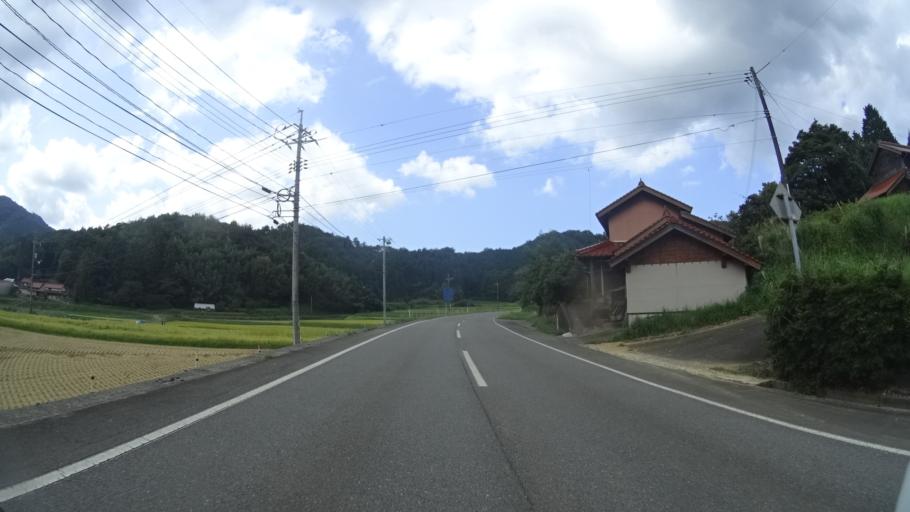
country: JP
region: Yamaguchi
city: Hagi
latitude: 34.5505
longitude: 131.6118
